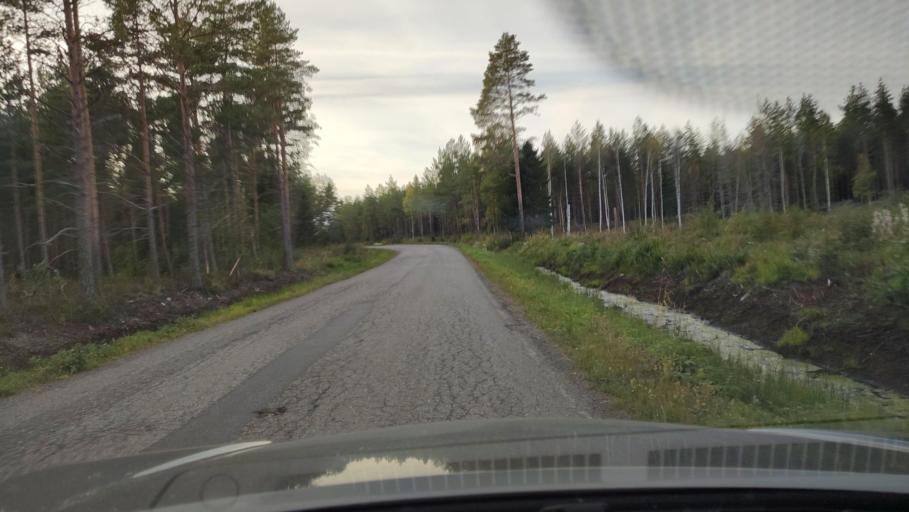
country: FI
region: Ostrobothnia
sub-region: Sydosterbotten
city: Kristinestad
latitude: 62.1498
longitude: 21.5504
